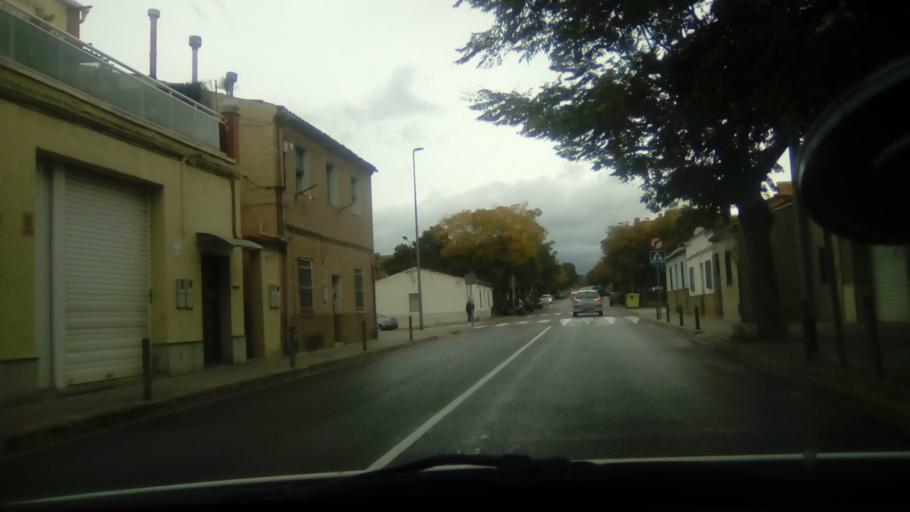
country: ES
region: Catalonia
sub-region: Provincia de Barcelona
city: Monistrol de Montserrat
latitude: 41.6715
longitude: 1.8625
